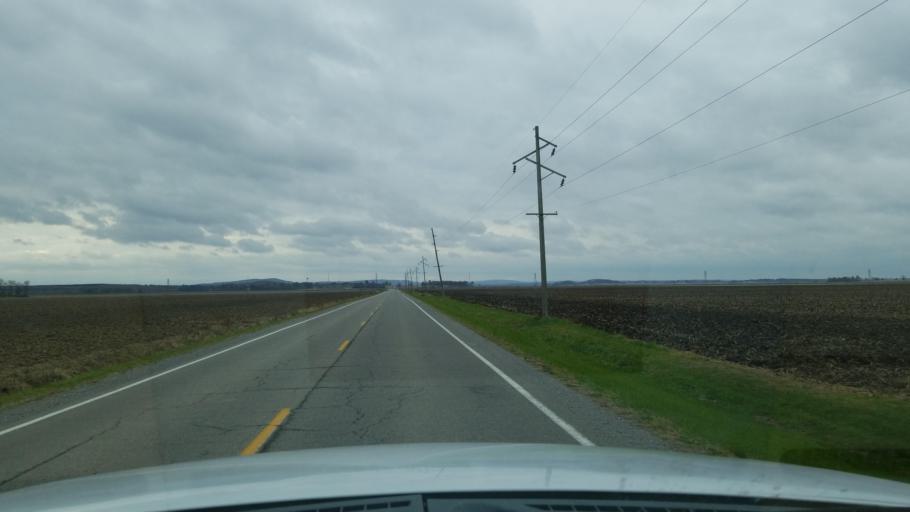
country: US
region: Illinois
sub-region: Saline County
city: Eldorado
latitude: 37.7826
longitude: -88.4383
